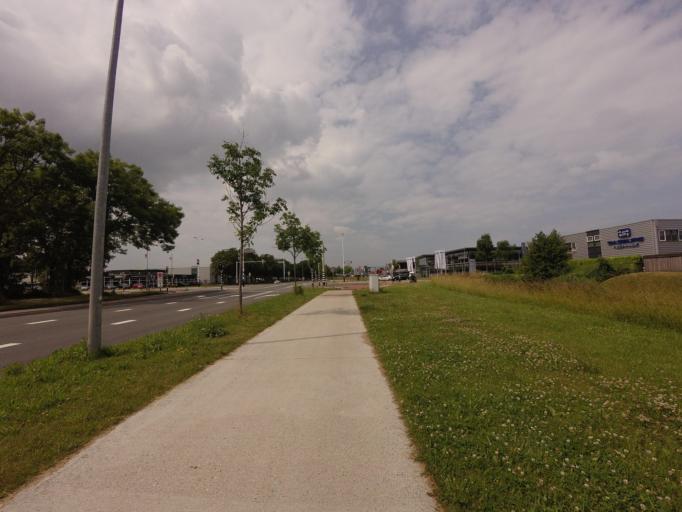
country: NL
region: North Holland
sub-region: Gemeente Hoorn
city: Hoorn
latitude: 52.6672
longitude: 5.0625
